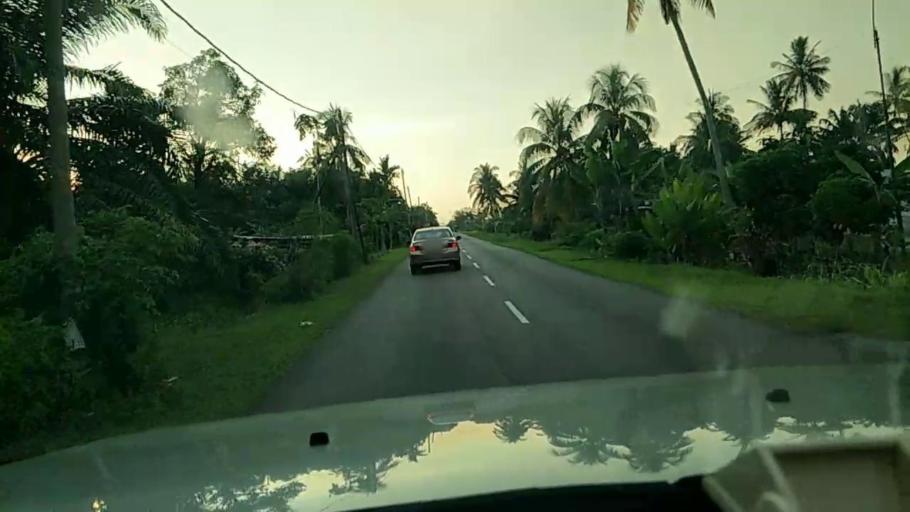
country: MY
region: Selangor
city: Kuala Selangor
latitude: 3.3147
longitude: 101.2834
